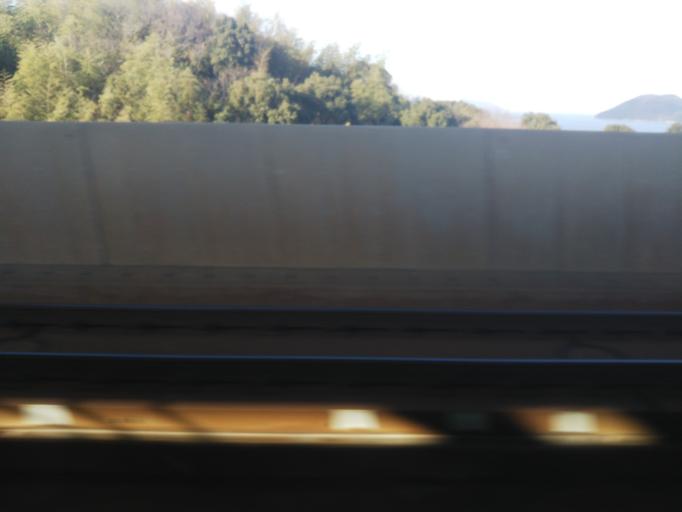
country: JP
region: Kagawa
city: Sakaidecho
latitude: 34.4167
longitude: 133.8048
